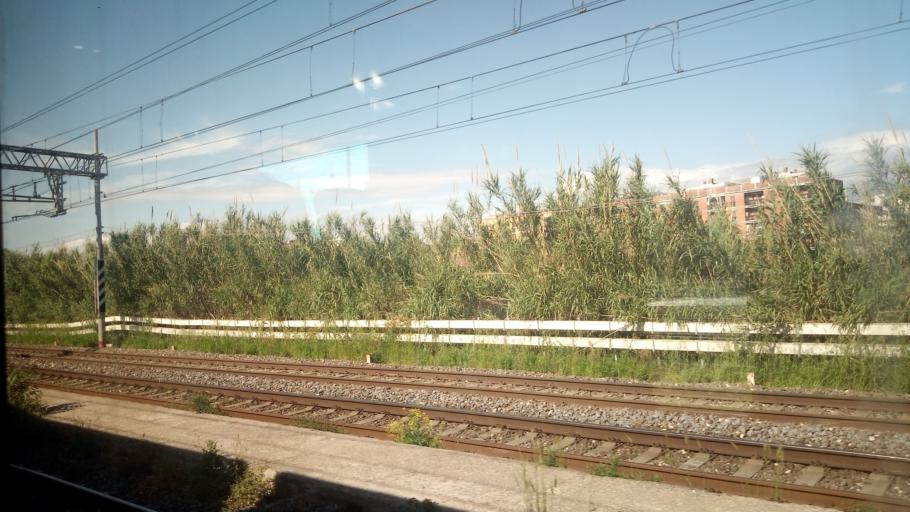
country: IT
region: Latium
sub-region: Citta metropolitana di Roma Capitale
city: Rome
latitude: 41.8746
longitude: 12.5385
